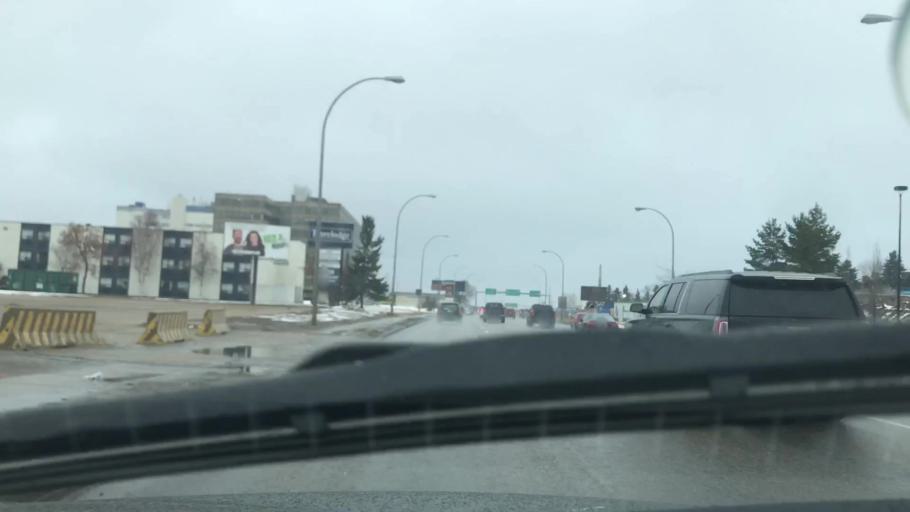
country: CA
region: Alberta
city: Edmonton
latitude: 53.4848
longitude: -113.4948
